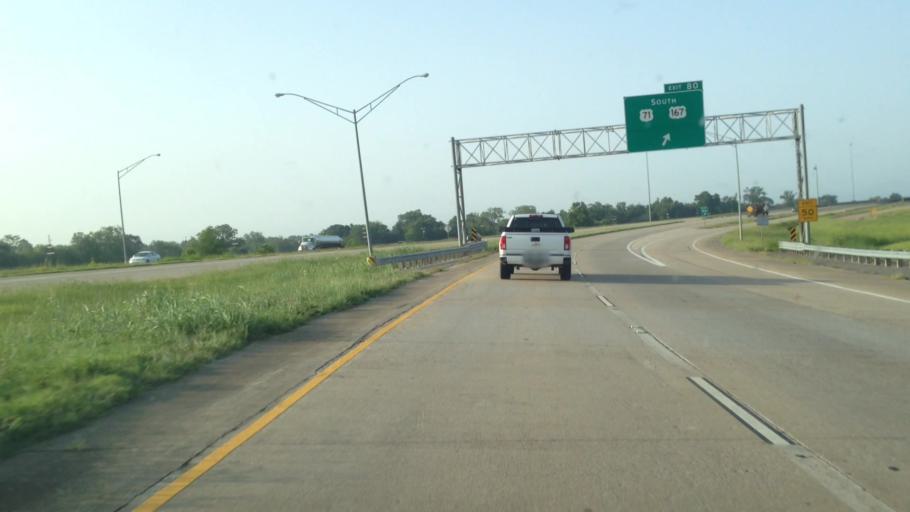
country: US
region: Louisiana
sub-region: Rapides Parish
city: Alexandria
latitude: 31.2483
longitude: -92.4292
